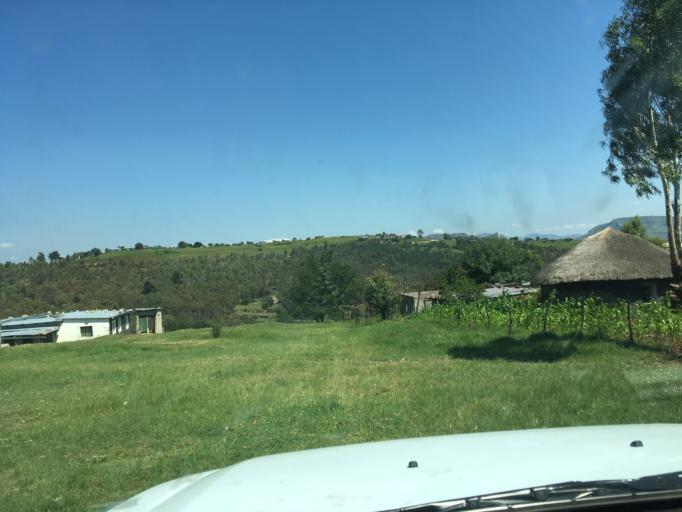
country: LS
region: Butha-Buthe
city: Butha-Buthe
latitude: -28.7233
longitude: 28.3675
